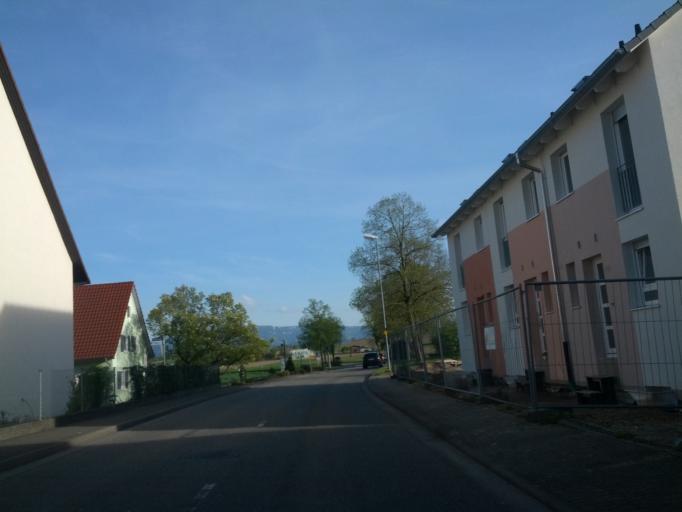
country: DE
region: Baden-Wuerttemberg
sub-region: Freiburg Region
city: Umkirch
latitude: 48.0685
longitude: 7.7992
